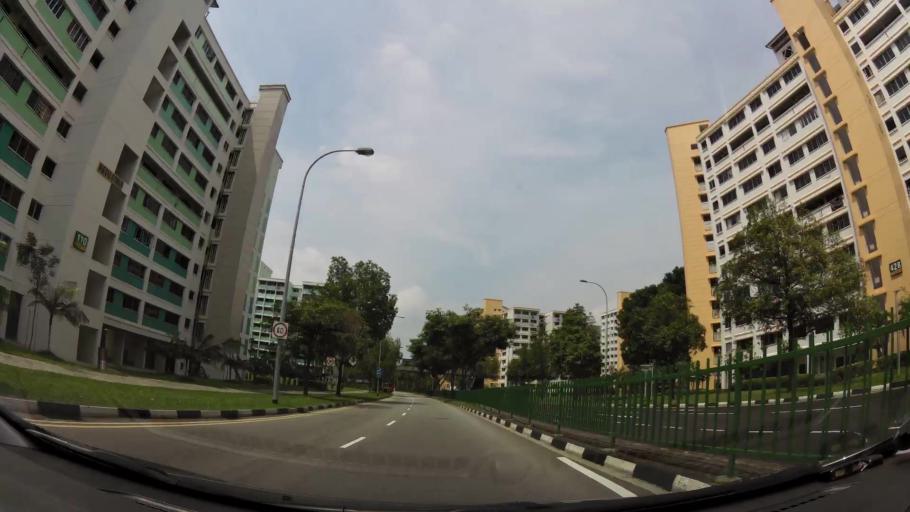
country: MY
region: Johor
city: Kampung Pasir Gudang Baru
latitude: 1.3690
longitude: 103.9566
